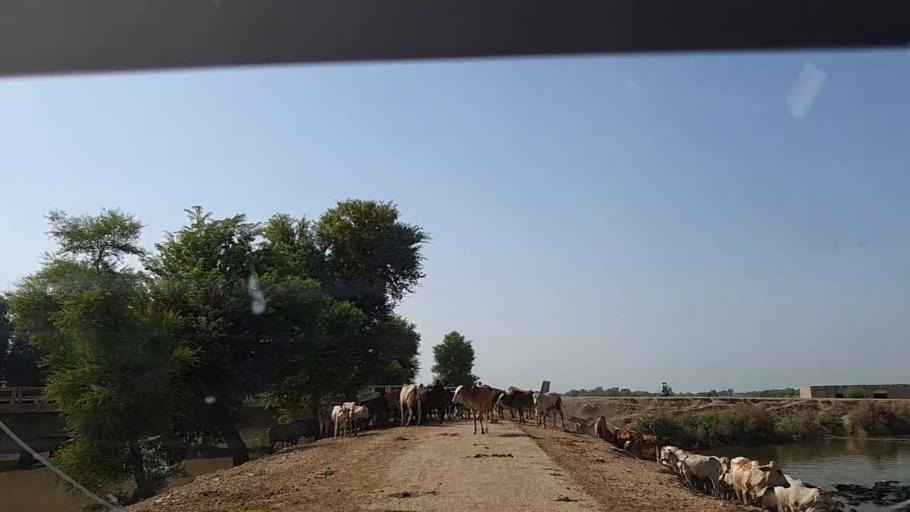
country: PK
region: Sindh
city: Ghauspur
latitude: 28.2008
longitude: 69.0414
